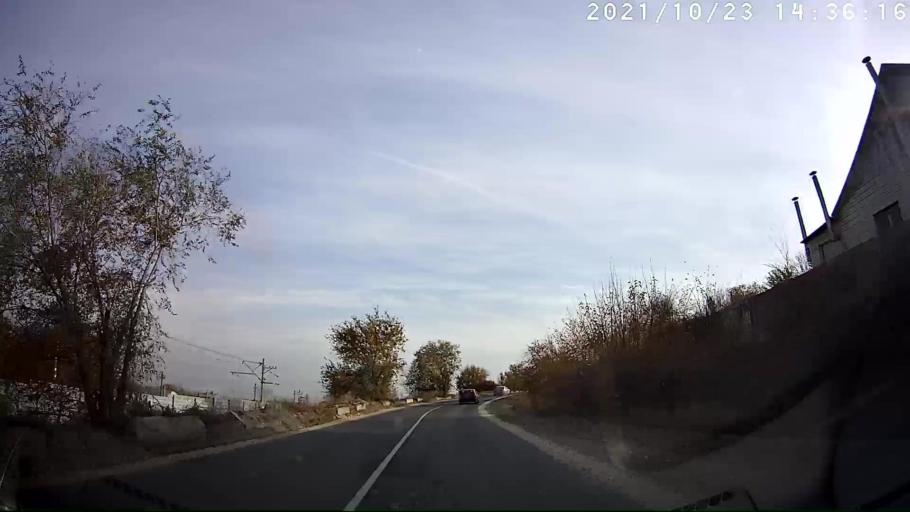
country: RU
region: Volgograd
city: Krasnoslobodsk
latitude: 48.5041
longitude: 44.5402
